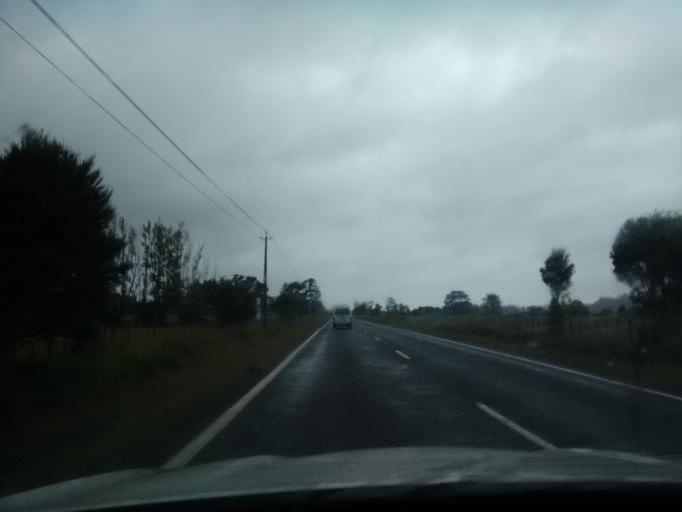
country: NZ
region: Waikato
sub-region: Thames-Coromandel District
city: Whitianga
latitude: -36.8555
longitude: 175.6525
